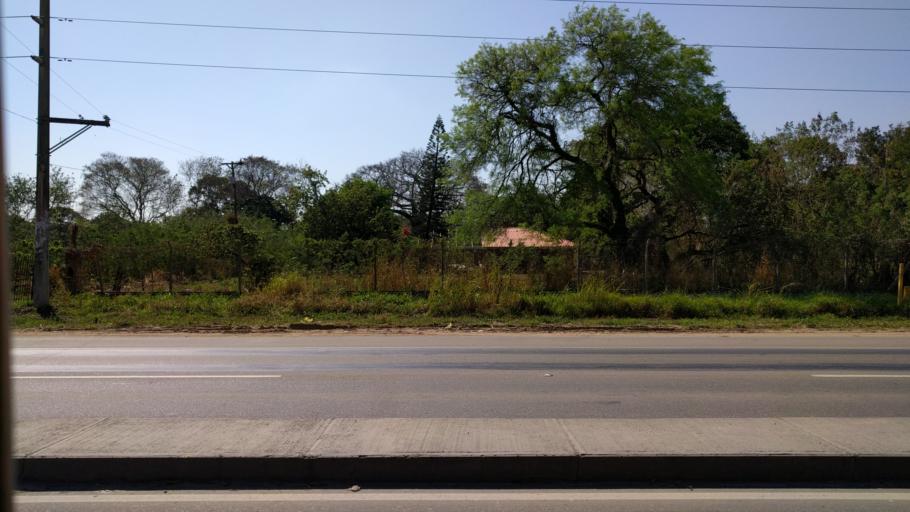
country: BO
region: Santa Cruz
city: Cotoca
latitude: -17.7647
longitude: -63.0744
